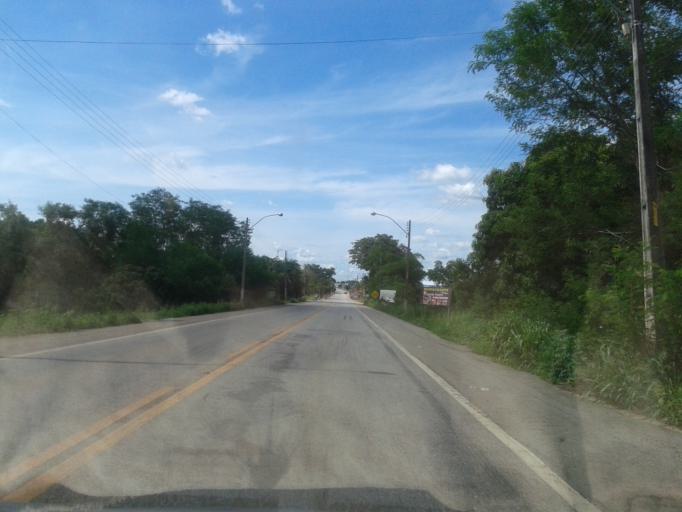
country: BR
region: Goias
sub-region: Itapuranga
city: Itapuranga
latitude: -15.4576
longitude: -50.3580
